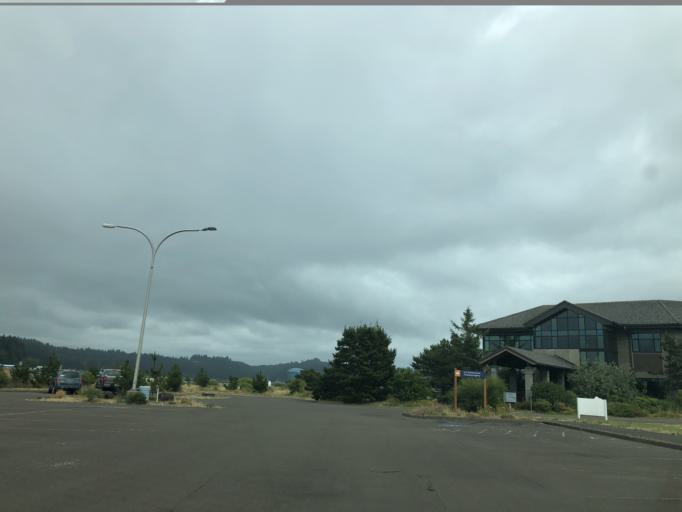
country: US
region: Oregon
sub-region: Lincoln County
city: Newport
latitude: 44.6231
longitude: -124.0440
